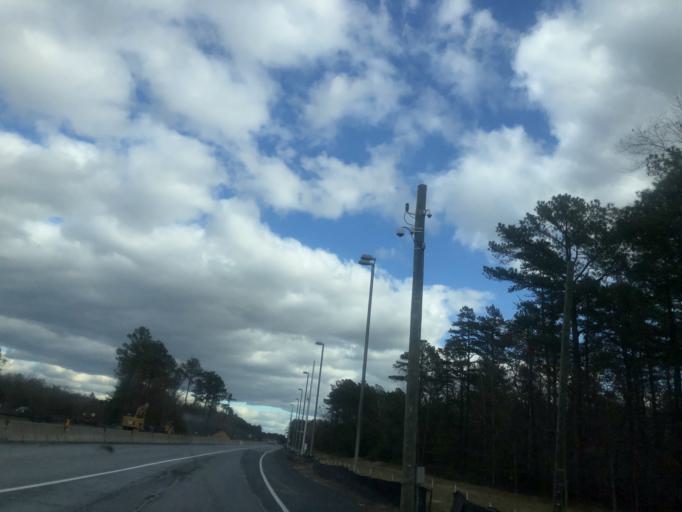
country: US
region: New Jersey
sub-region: Ocean County
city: Mystic Island
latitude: 39.6134
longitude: -74.4235
